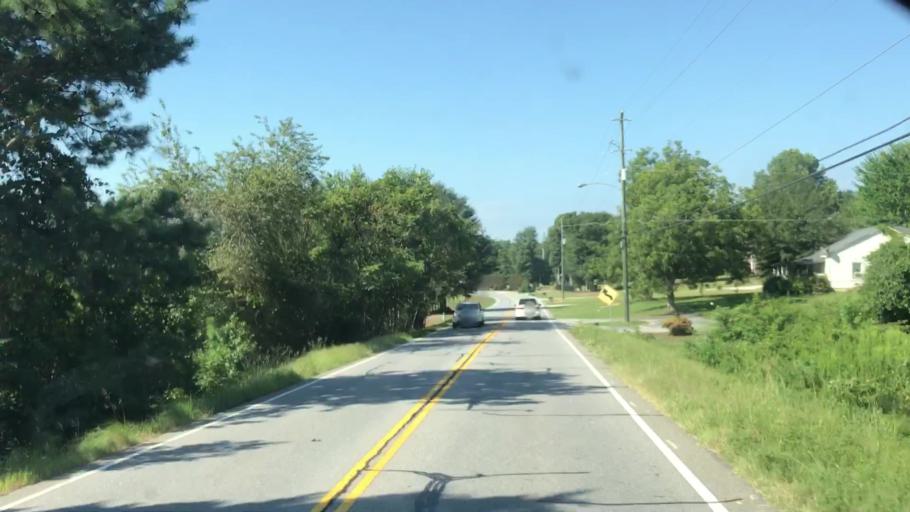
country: US
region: Georgia
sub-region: Walton County
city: Loganville
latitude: 33.8519
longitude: -83.8918
